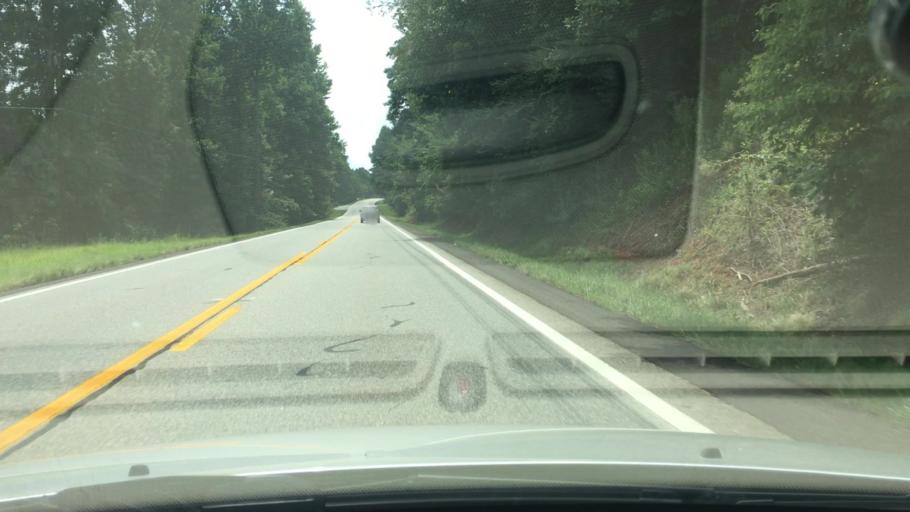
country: US
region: Georgia
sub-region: Lumpkin County
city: Dahlonega
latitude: 34.4978
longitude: -83.9401
